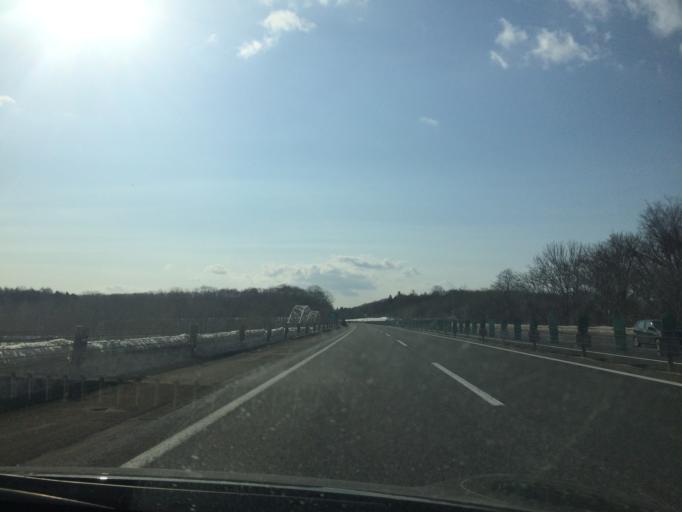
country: JP
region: Hokkaido
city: Chitose
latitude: 42.8642
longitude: 141.5578
